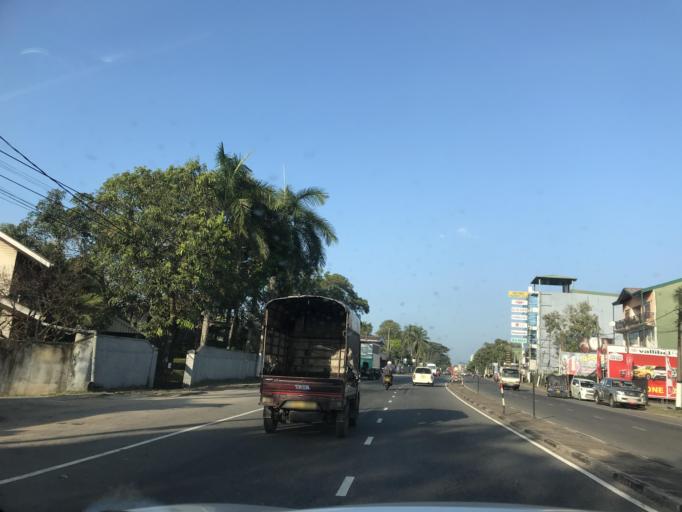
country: LK
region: Western
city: Ja Ela
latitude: 7.0888
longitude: 79.8993
